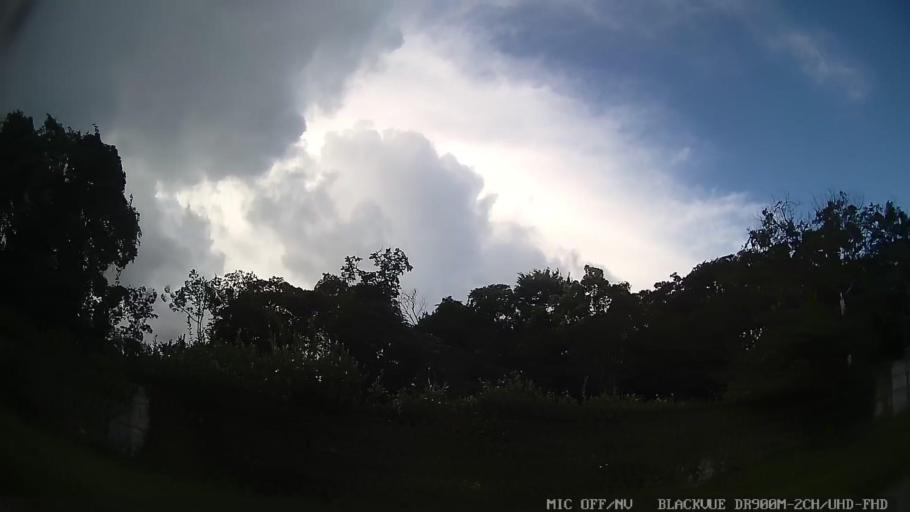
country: BR
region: Sao Paulo
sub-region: Peruibe
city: Peruibe
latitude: -24.2028
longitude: -46.9336
